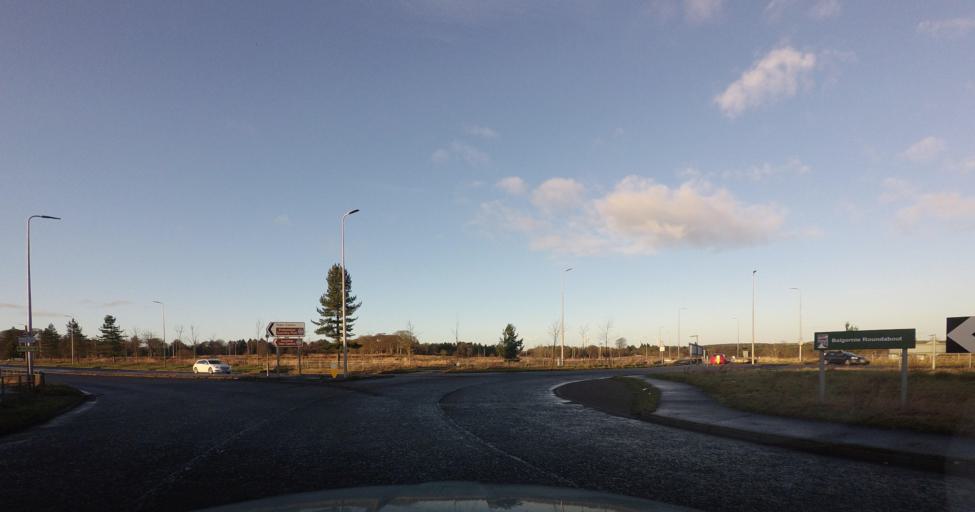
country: GB
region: Scotland
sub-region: West Lothian
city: Armadale
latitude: 55.8683
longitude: -3.7047
